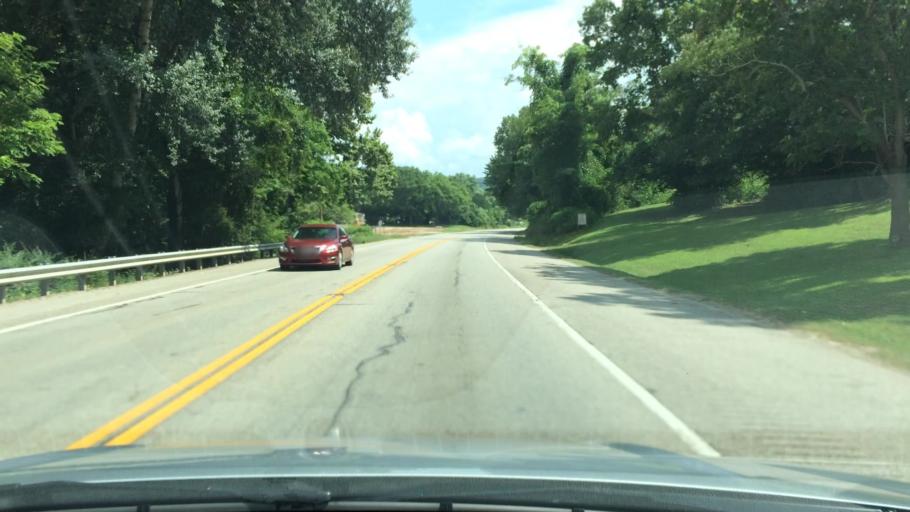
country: US
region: Kentucky
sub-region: Pulaski County
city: Somerset
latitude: 36.9639
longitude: -84.5846
